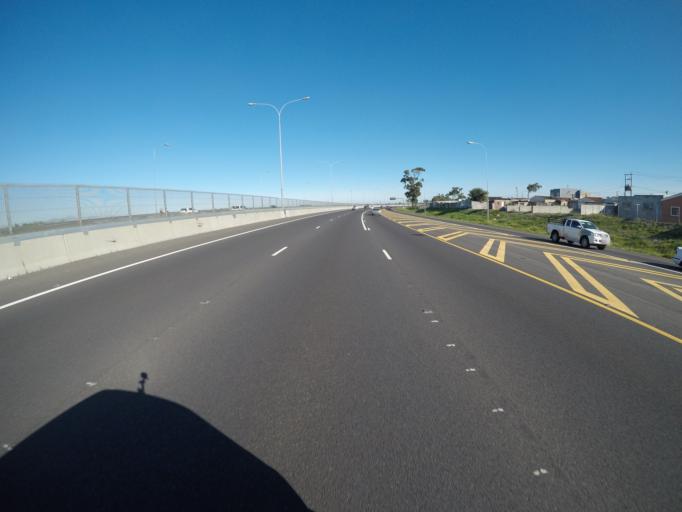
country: ZA
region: Western Cape
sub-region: City of Cape Town
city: Kraaifontein
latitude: -33.9814
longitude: 18.6518
